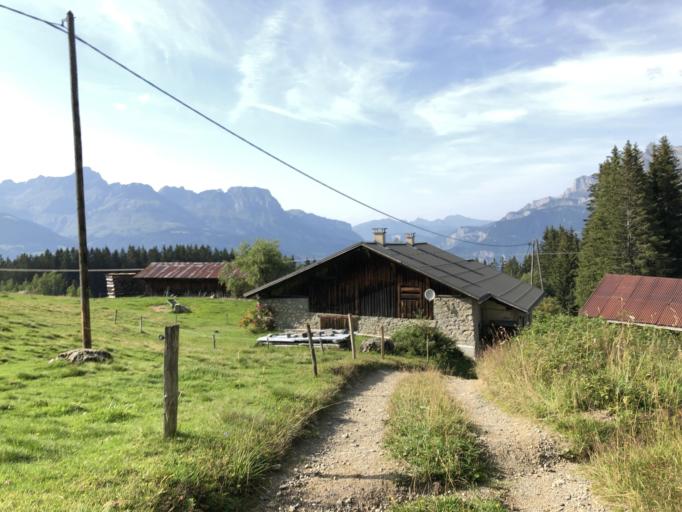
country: FR
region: Rhone-Alpes
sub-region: Departement de la Haute-Savoie
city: Combloux
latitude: 45.8754
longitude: 6.6610
